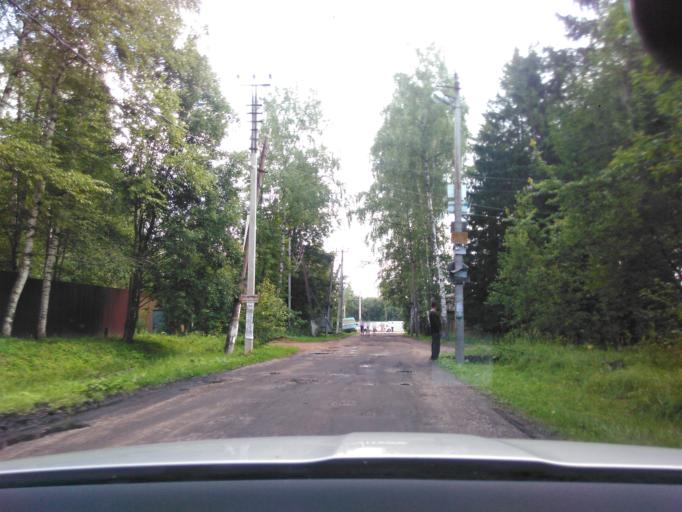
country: RU
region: Moskovskaya
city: Radumlya
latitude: 56.1300
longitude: 37.2123
